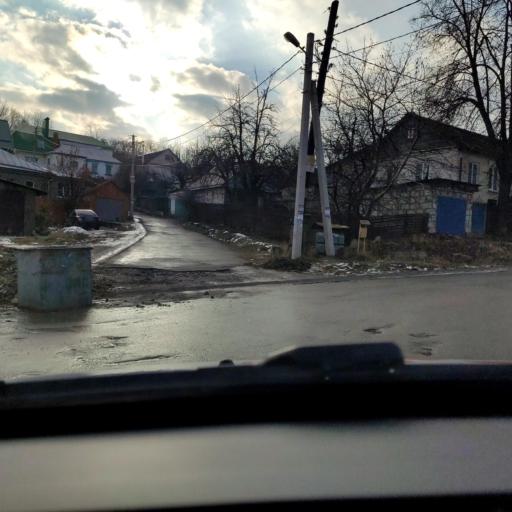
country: RU
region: Voronezj
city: Voronezh
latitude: 51.6298
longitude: 39.1844
